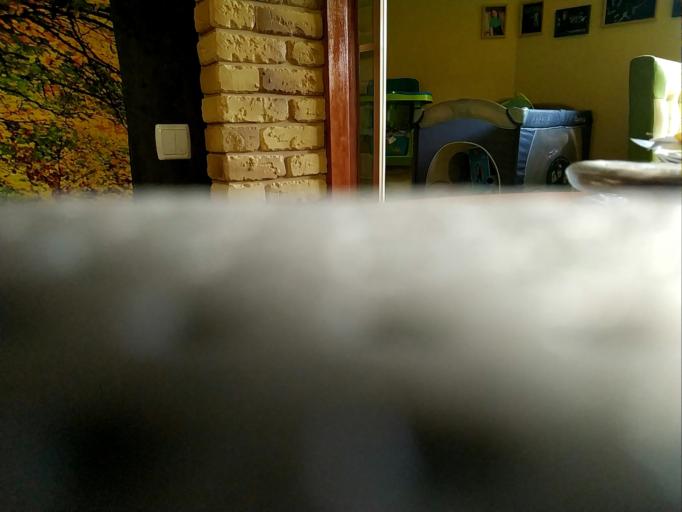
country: RU
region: Kaluga
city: Seredeyskiy
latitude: 53.9414
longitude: 35.3397
